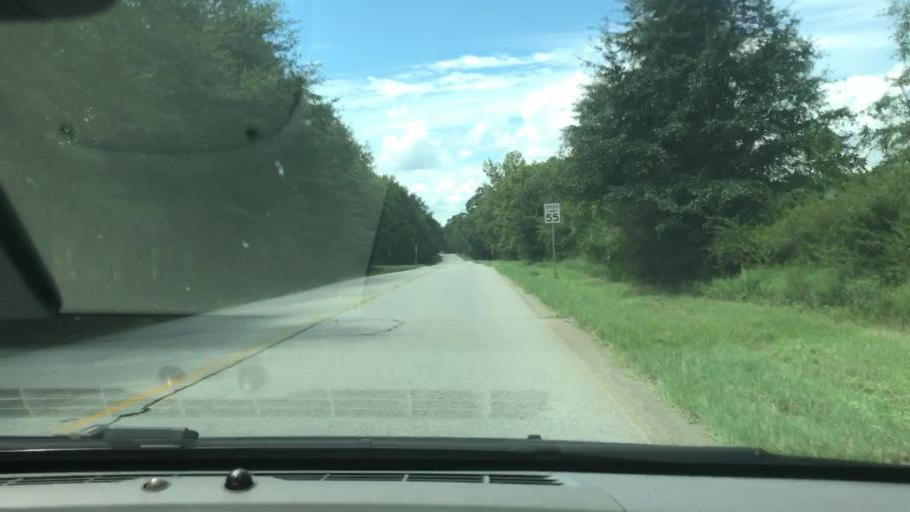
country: US
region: Georgia
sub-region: Stewart County
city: Lumpkin
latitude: 32.1464
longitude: -84.8320
